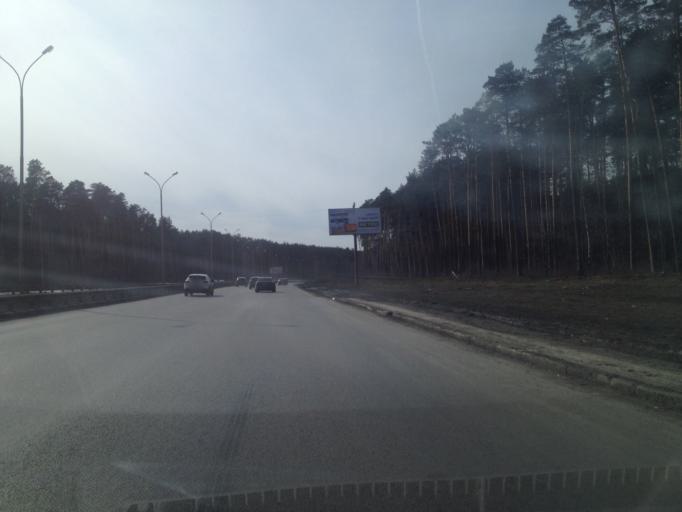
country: RU
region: Sverdlovsk
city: Sovkhoznyy
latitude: 56.7892
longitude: 60.5897
